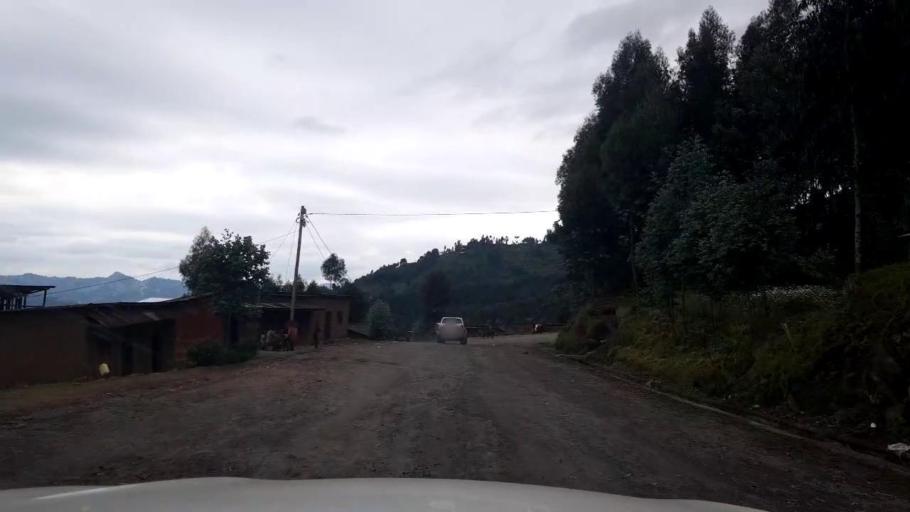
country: RW
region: Northern Province
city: Musanze
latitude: -1.5042
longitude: 29.5335
